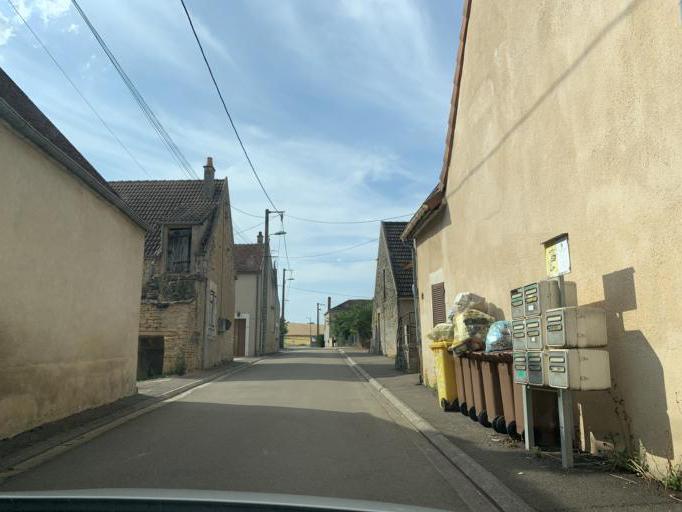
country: FR
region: Bourgogne
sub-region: Departement de l'Yonne
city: Fontenailles
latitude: 47.4815
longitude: 3.4208
